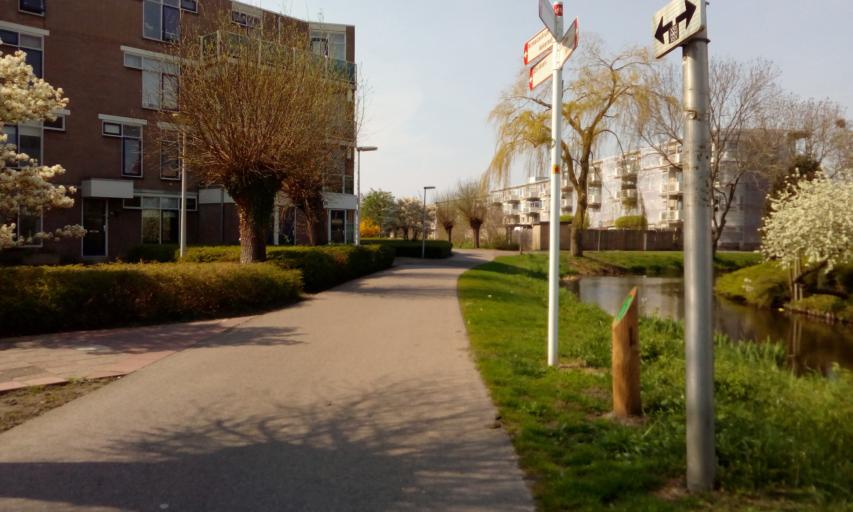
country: NL
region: South Holland
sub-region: Gemeente Spijkenisse
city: Spijkenisse
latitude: 51.8309
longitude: 4.3223
